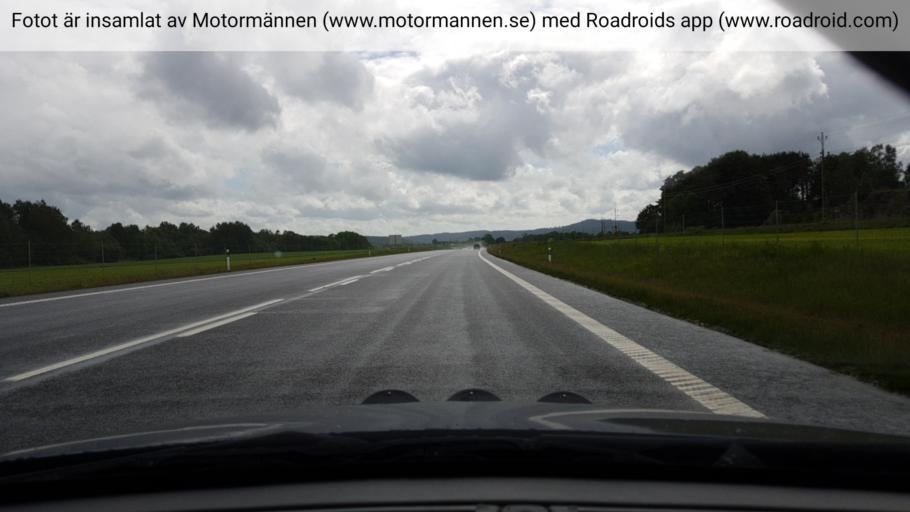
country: SE
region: Vaestra Goetaland
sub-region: Marks Kommun
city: Kinna
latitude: 57.4524
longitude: 12.5760
